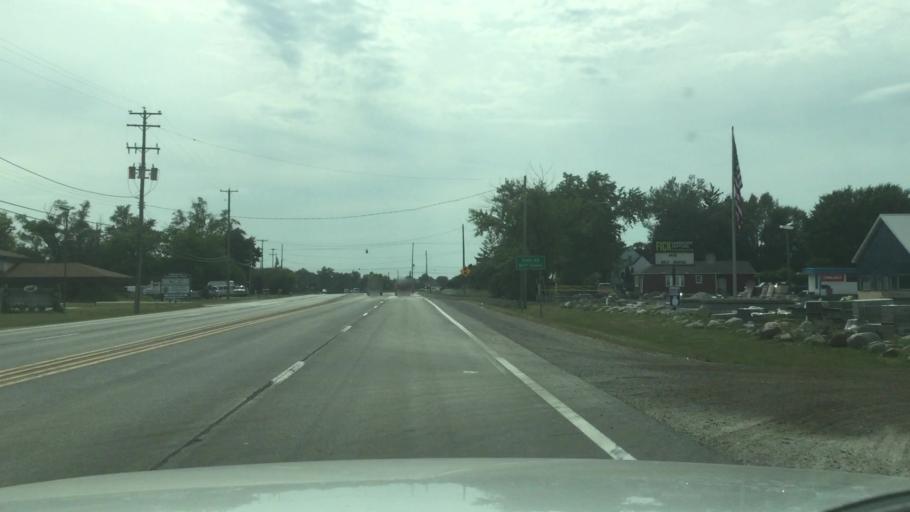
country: US
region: Michigan
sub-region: Genesee County
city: Swartz Creek
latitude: 43.0014
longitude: -83.8088
